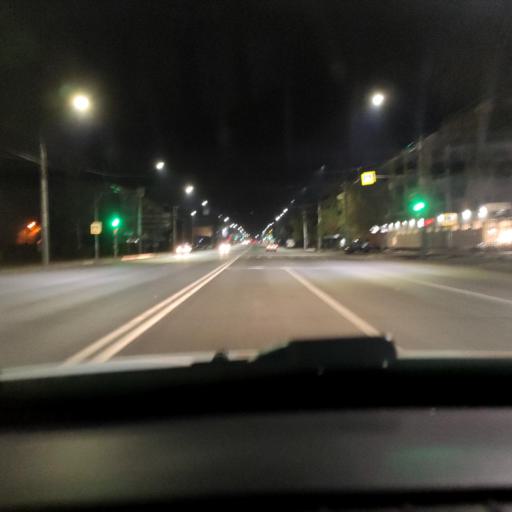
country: RU
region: Voronezj
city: Voronezh
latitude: 51.6663
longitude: 39.2495
